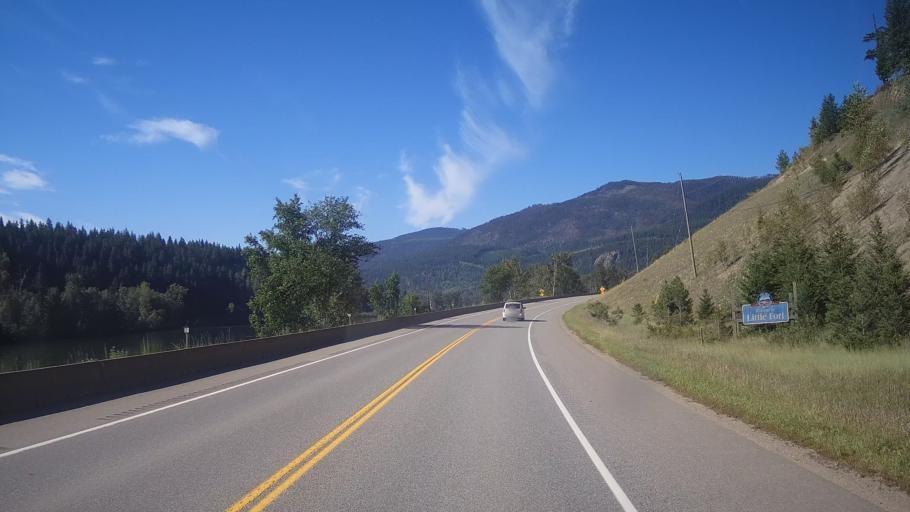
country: CA
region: British Columbia
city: Kamloops
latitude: 51.4323
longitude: -120.1944
